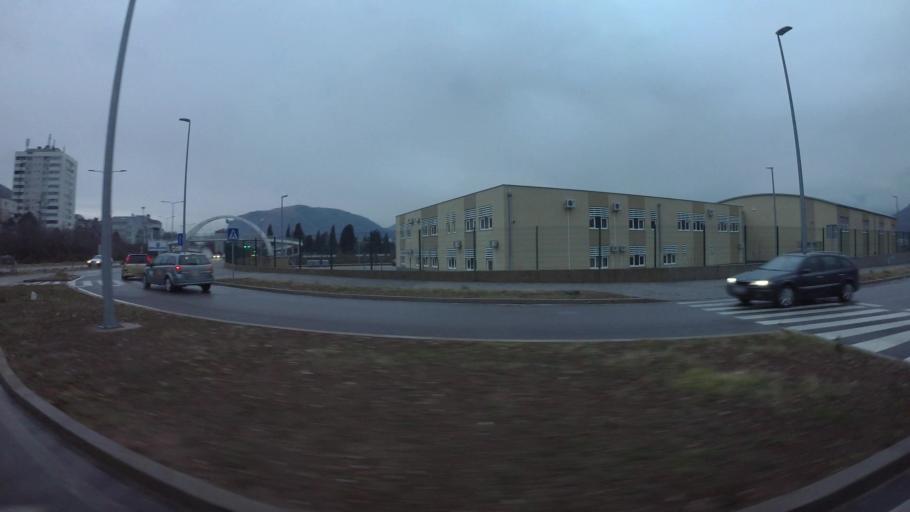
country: BA
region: Federation of Bosnia and Herzegovina
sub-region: Hercegovacko-Bosanski Kanton
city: Mostar
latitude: 43.3579
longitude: 17.8126
